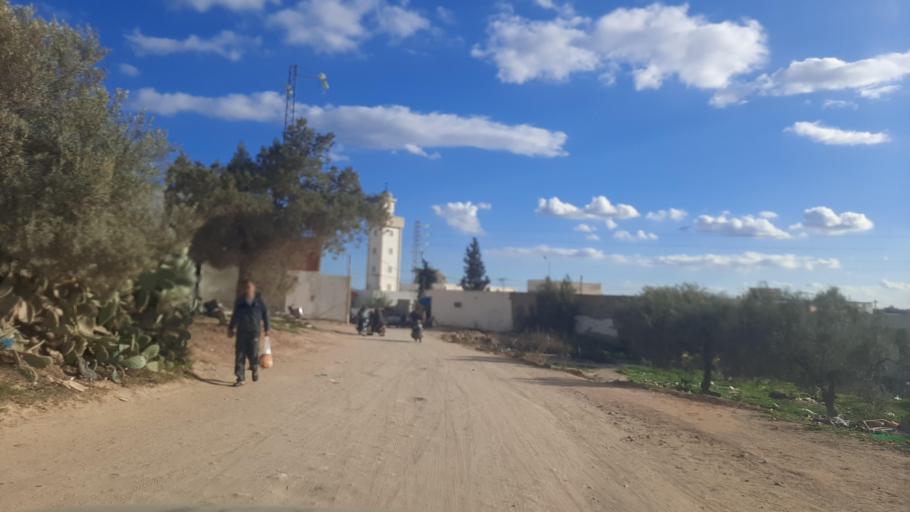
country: TN
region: Nabul
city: Al Hammamat
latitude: 36.4175
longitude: 10.5148
